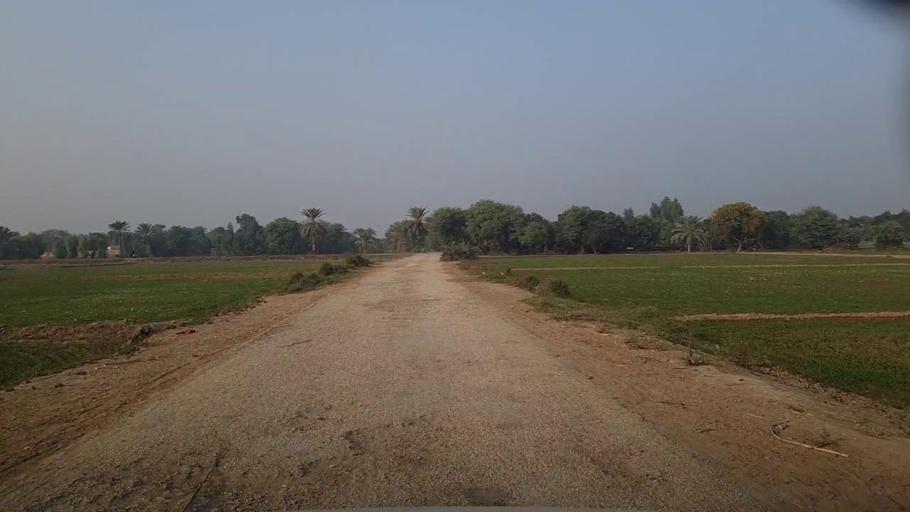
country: PK
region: Sindh
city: Kandiari
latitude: 27.0089
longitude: 68.4614
